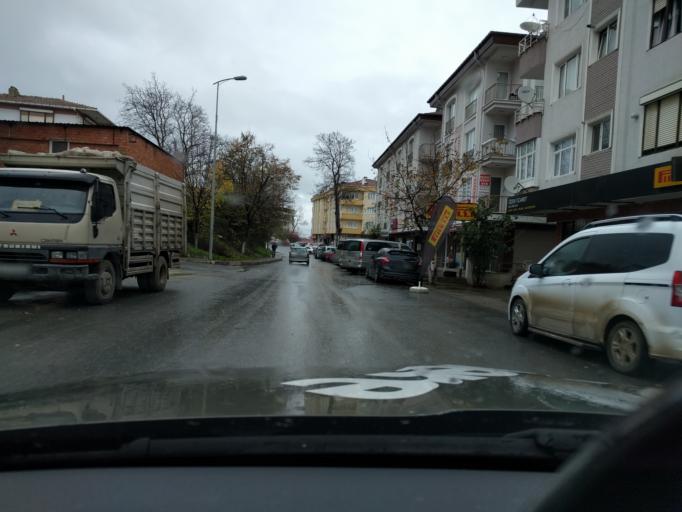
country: TR
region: Istanbul
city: Catalca
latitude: 41.1449
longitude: 28.4594
